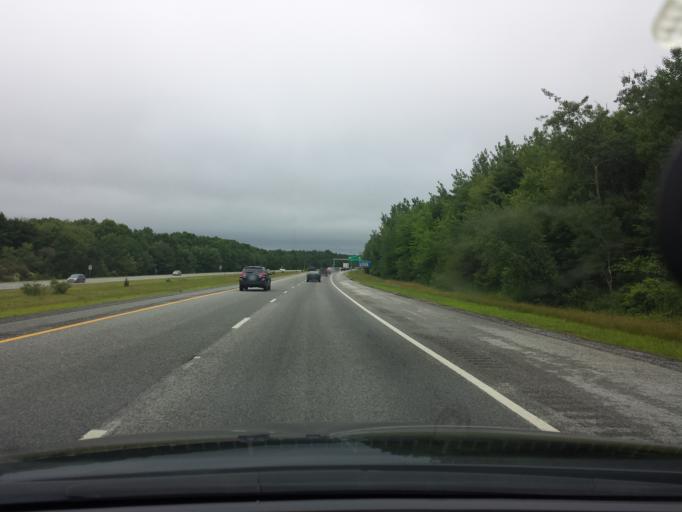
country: US
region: Rhode Island
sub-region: Kent County
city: West Greenwich
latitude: 41.5942
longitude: -71.6594
